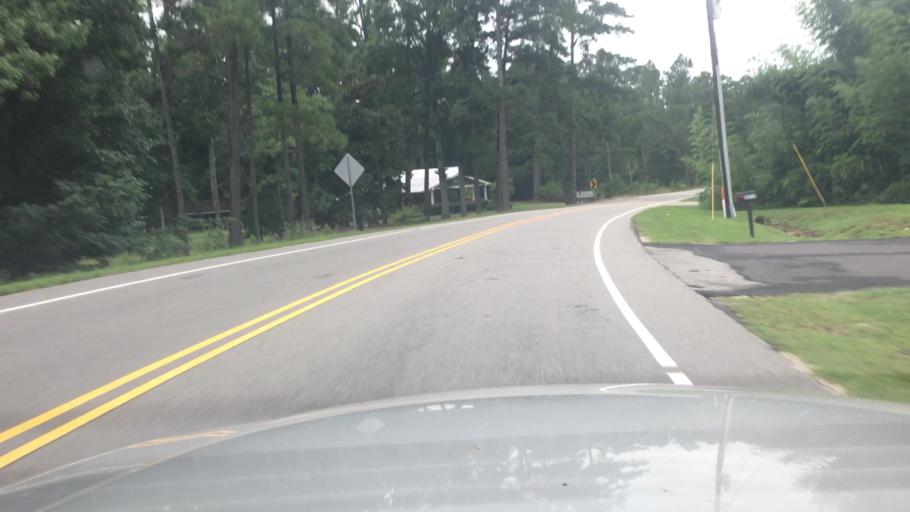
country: US
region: North Carolina
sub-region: Cumberland County
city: Hope Mills
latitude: 34.9678
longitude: -78.9163
